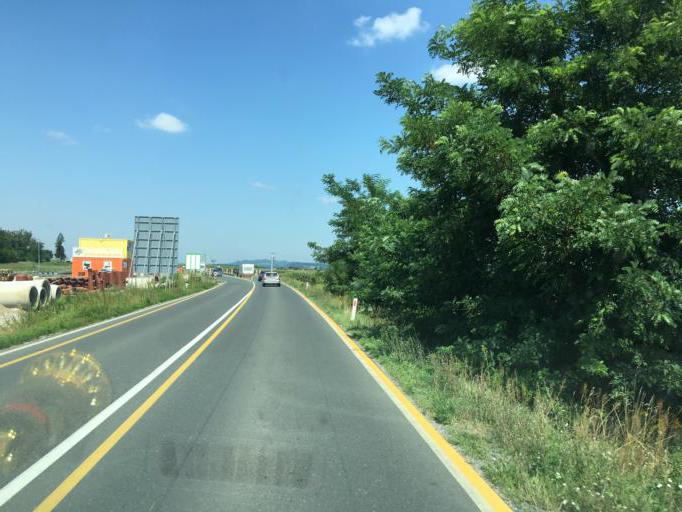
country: SI
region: Hajdina
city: Spodnja Hajdina
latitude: 46.3853
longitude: 15.8649
